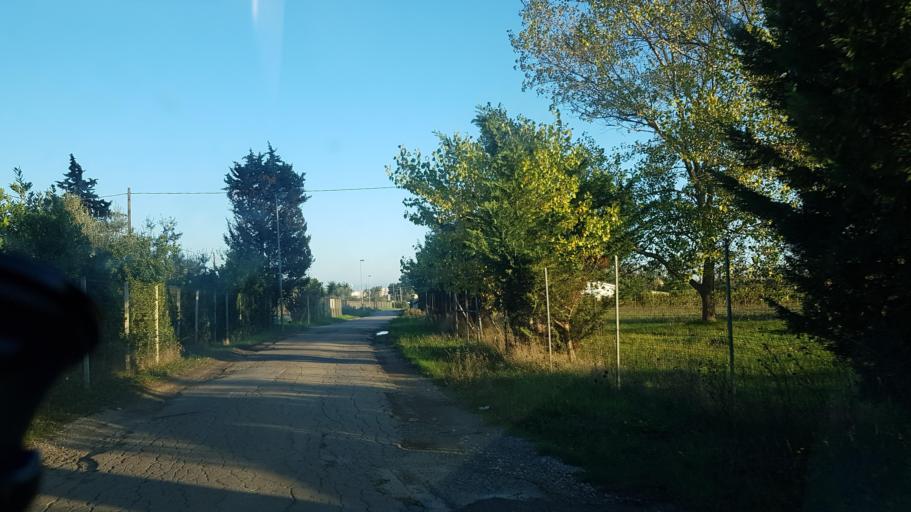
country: IT
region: Apulia
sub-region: Provincia di Brindisi
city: Mesagne
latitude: 40.5629
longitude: 17.7838
